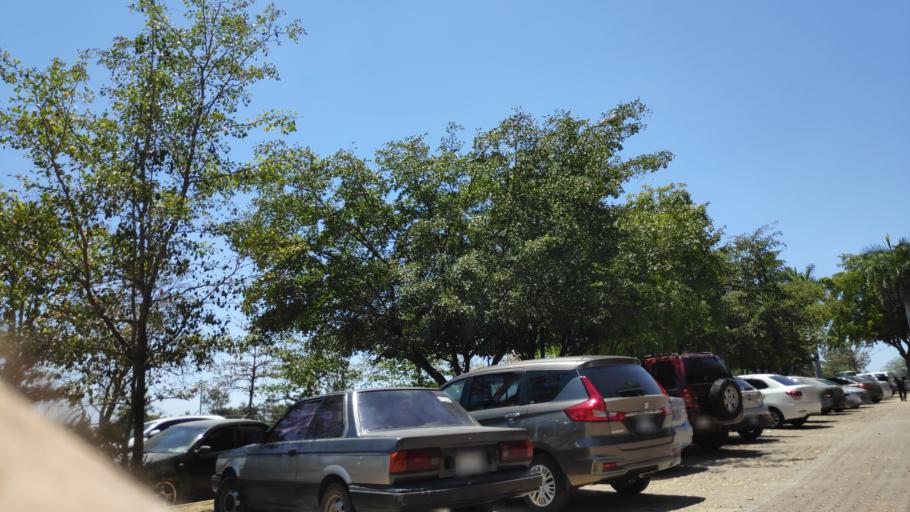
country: MX
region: Sinaloa
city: Culiacan
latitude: 24.8258
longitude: -107.3800
